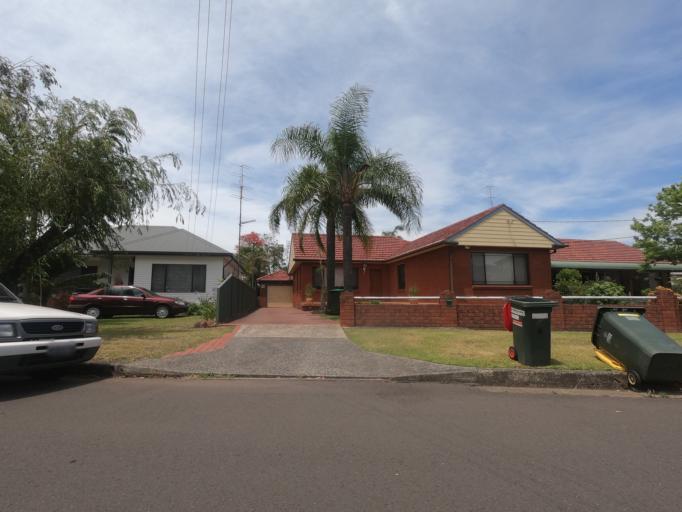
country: AU
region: New South Wales
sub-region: Wollongong
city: Fairy Meadow
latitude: -34.3897
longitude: 150.8862
